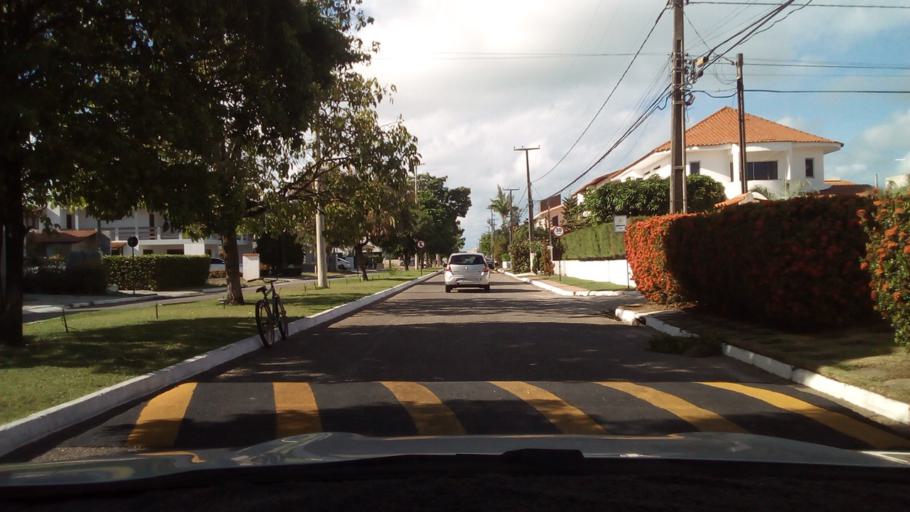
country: BR
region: Paraiba
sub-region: Joao Pessoa
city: Joao Pessoa
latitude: -7.1599
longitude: -34.8067
